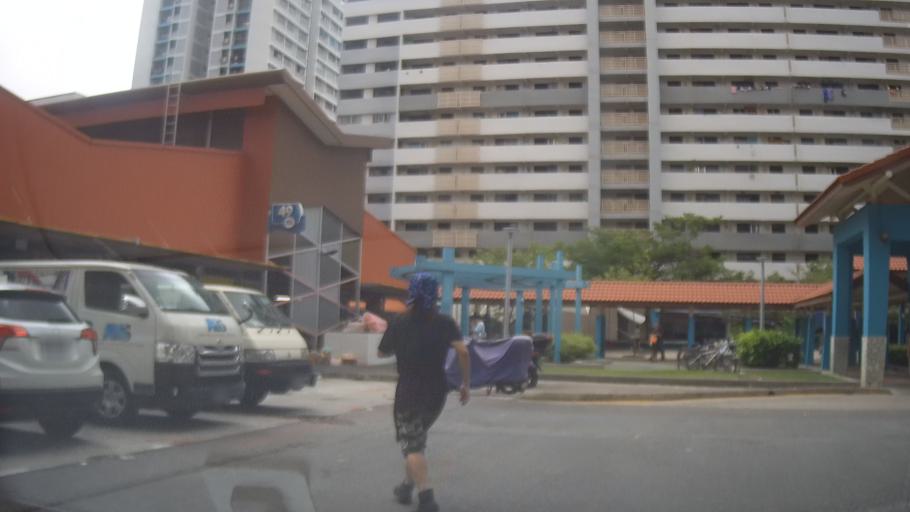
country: SG
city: Singapore
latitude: 1.3174
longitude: 103.8792
